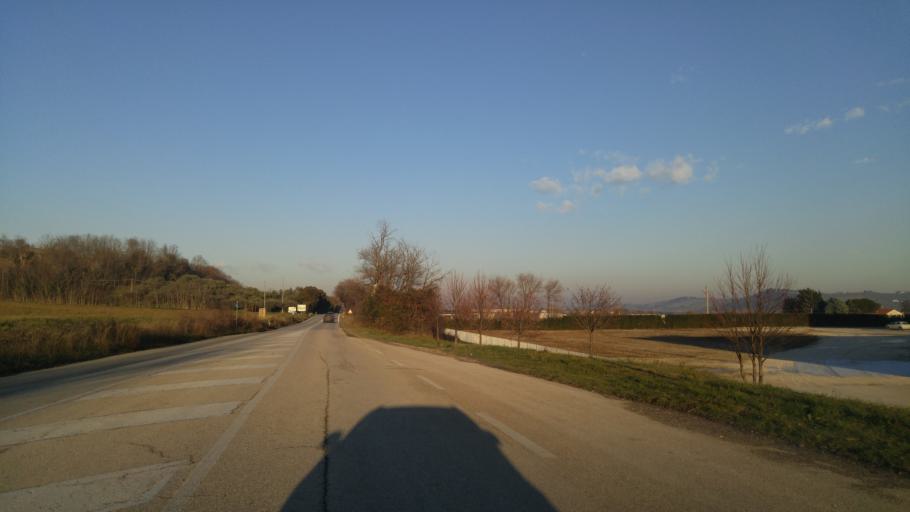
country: IT
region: The Marches
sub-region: Provincia di Ancona
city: Monterado
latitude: 43.7052
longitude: 13.0685
